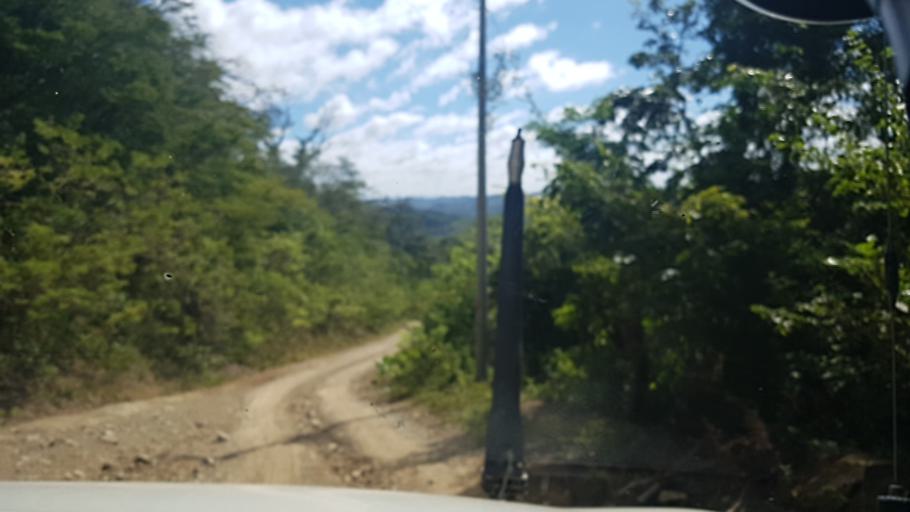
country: NI
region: Carazo
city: Santa Teresa
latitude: 11.6168
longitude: -86.1603
